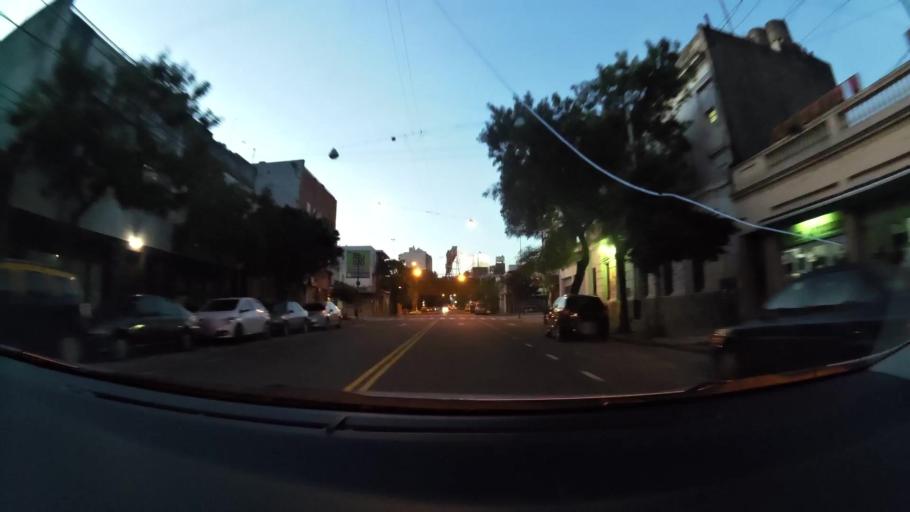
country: AR
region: Buenos Aires F.D.
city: Villa Santa Rita
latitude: -34.6408
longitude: -58.4572
